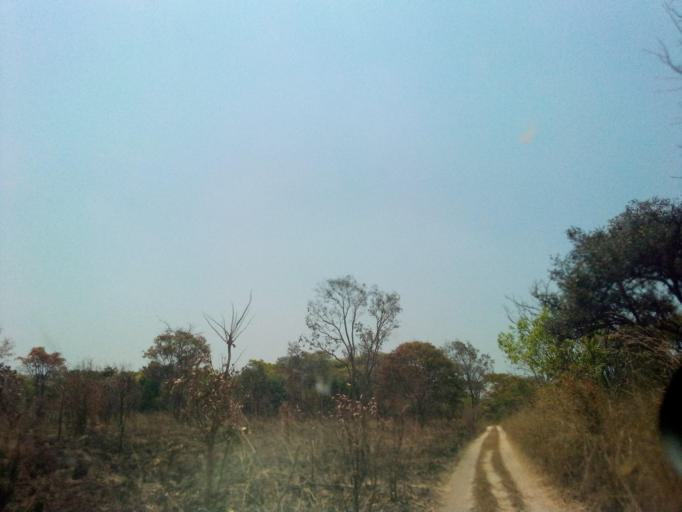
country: ZM
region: Copperbelt
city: Kataba
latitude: -12.2521
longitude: 30.3901
